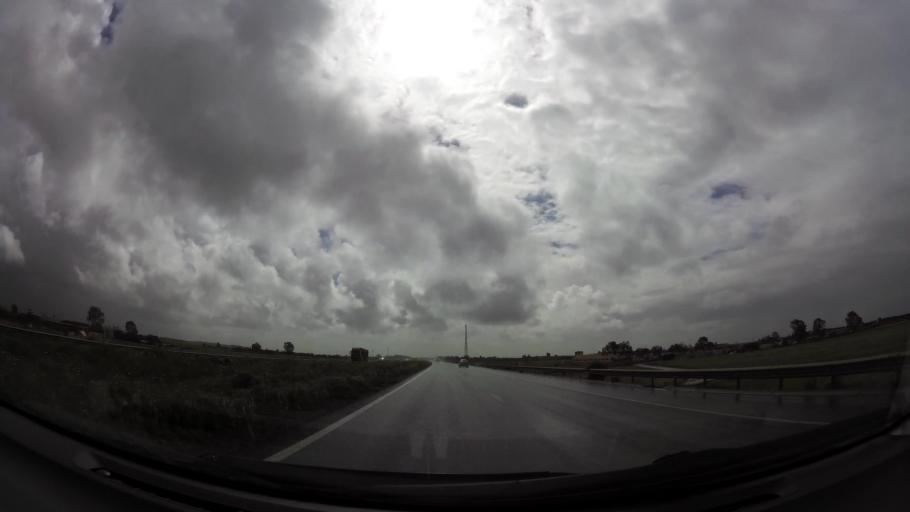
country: MA
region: Grand Casablanca
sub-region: Nouaceur
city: Dar Bouazza
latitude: 33.3894
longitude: -7.8776
